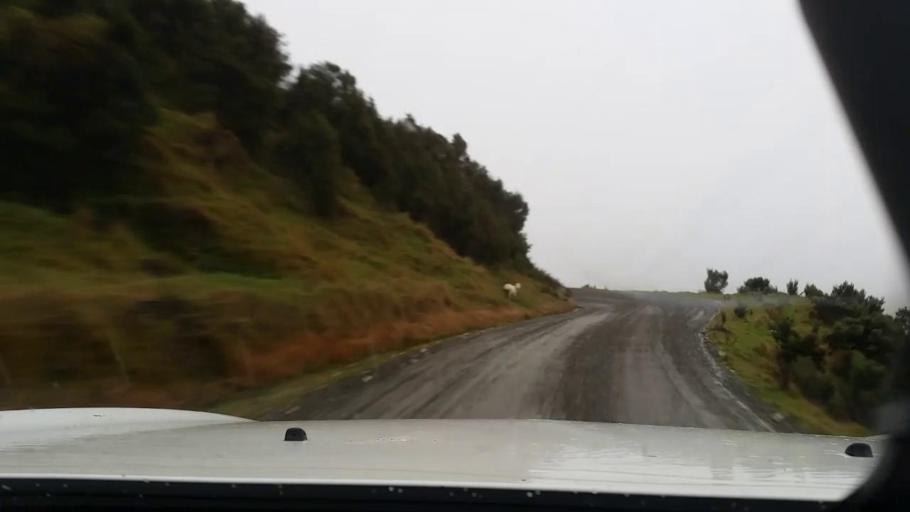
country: NZ
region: Wellington
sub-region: Masterton District
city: Masterton
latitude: -41.2479
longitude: 175.8799
